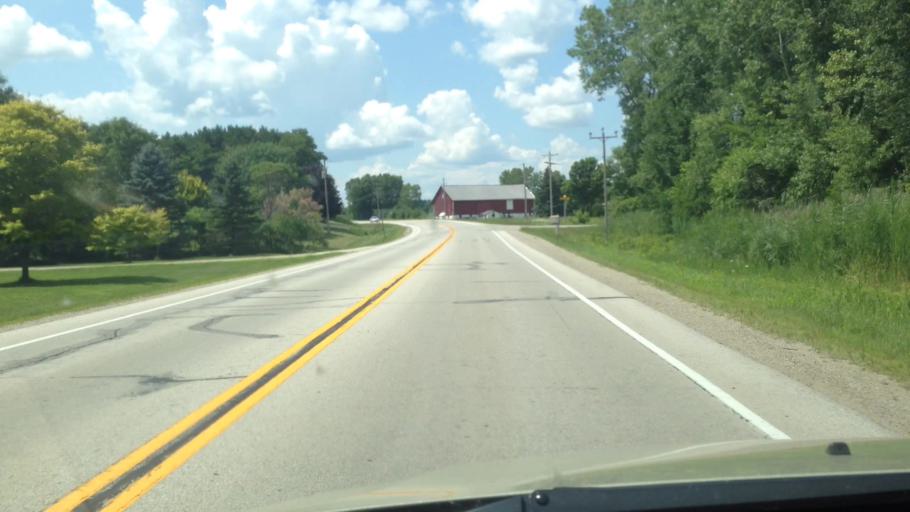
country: US
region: Wisconsin
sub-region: Brown County
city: Suamico
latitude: 44.6474
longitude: -88.1196
